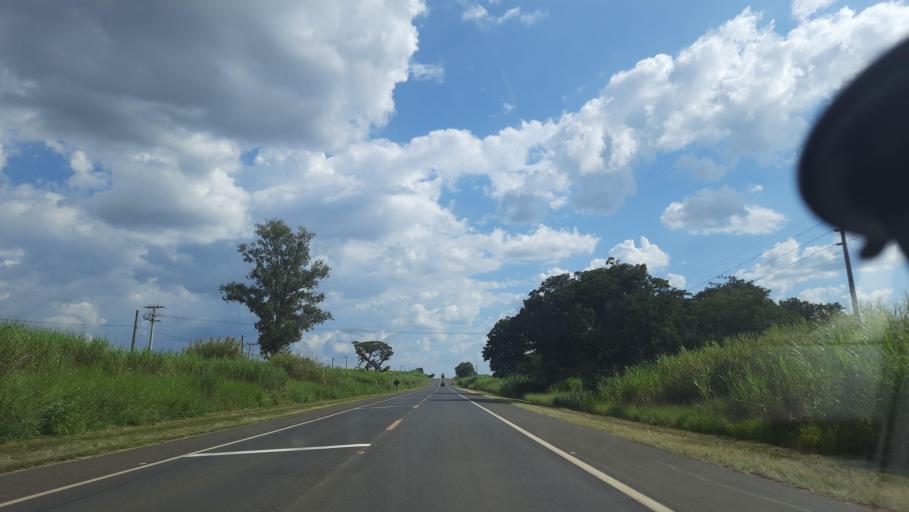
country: BR
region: Sao Paulo
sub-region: Sao Jose Do Rio Pardo
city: Sao Jose do Rio Pardo
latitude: -21.6702
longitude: -46.9220
